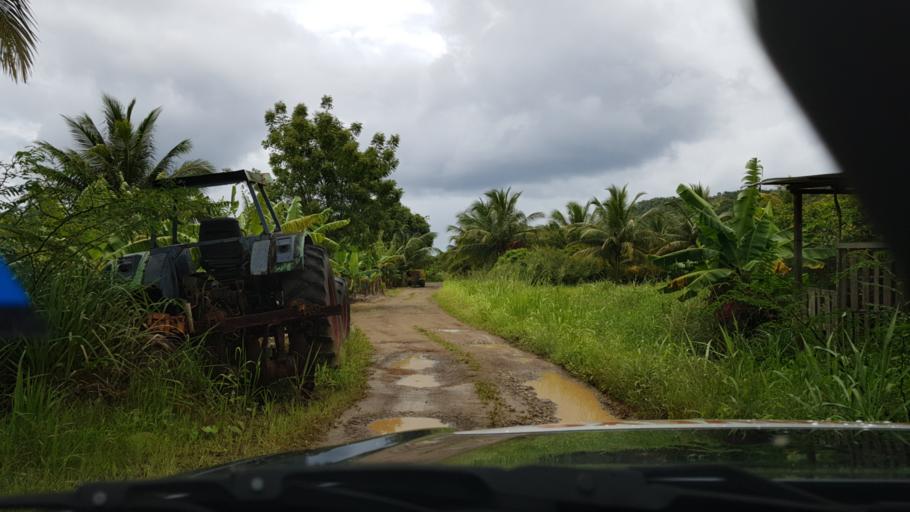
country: LC
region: Anse-la-Raye
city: Anse La Raye
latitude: 13.9508
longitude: -61.0215
